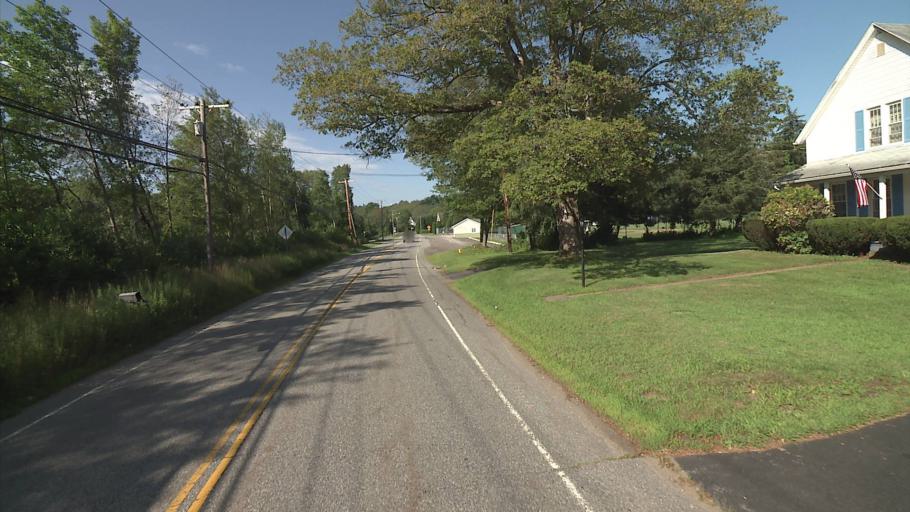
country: US
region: Connecticut
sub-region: New London County
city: Montville Center
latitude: 41.5515
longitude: -72.1689
